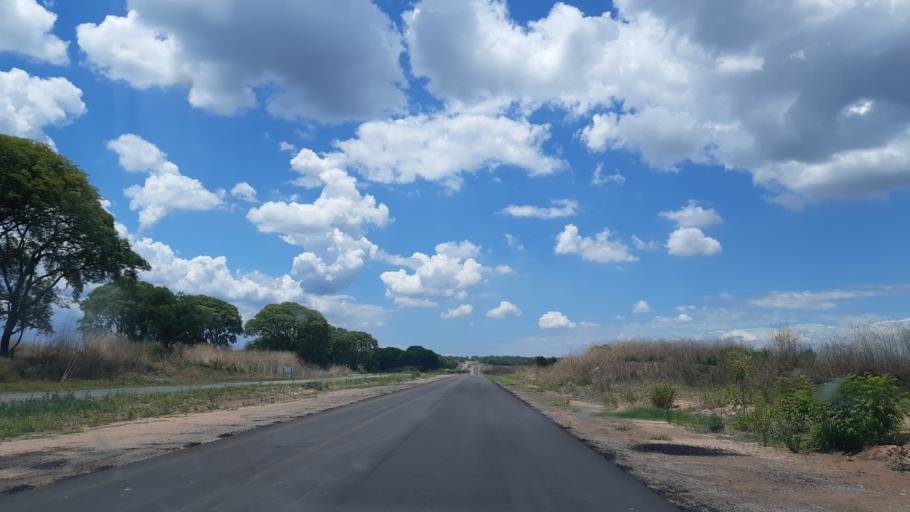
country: AR
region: Jujuy
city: La Mendieta
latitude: -24.3906
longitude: -64.9847
